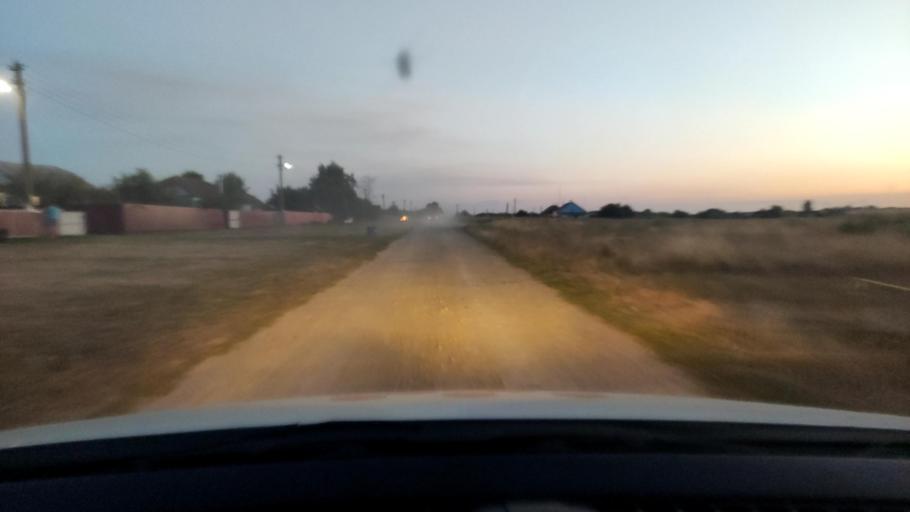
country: RU
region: Voronezj
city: Panino
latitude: 51.6533
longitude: 40.0213
